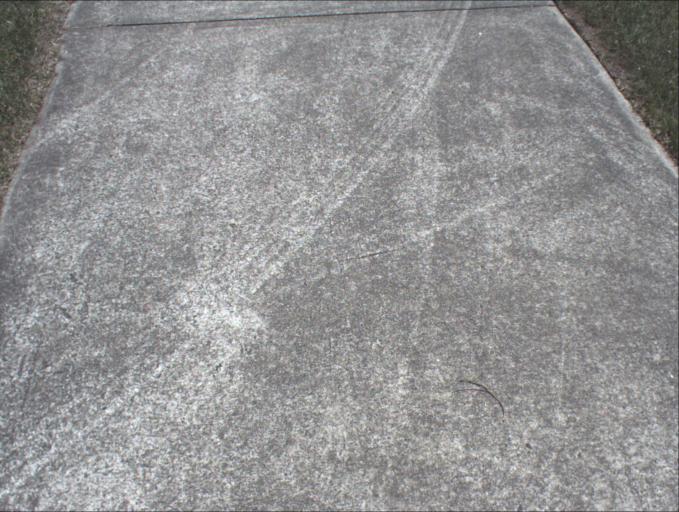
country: AU
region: Queensland
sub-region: Logan
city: Beenleigh
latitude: -27.6744
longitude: 153.1847
